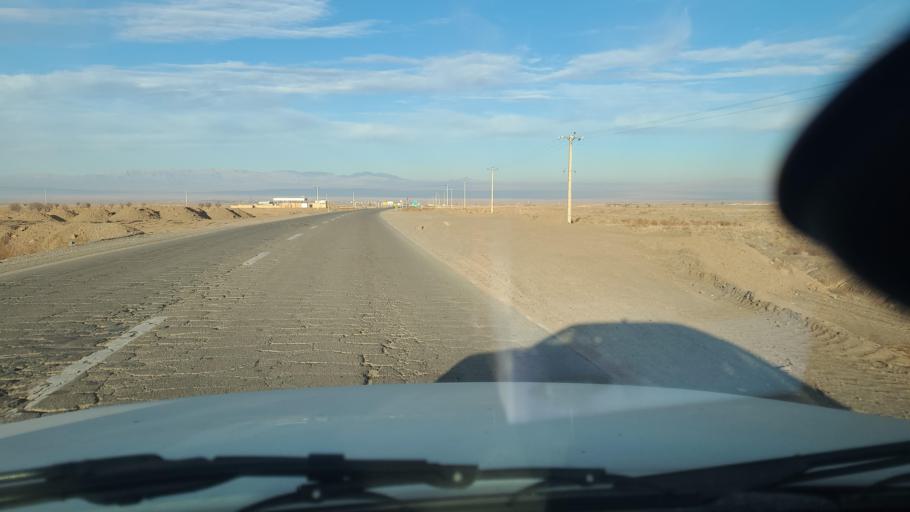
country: IR
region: Razavi Khorasan
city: Neqab
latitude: 36.5040
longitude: 57.5331
